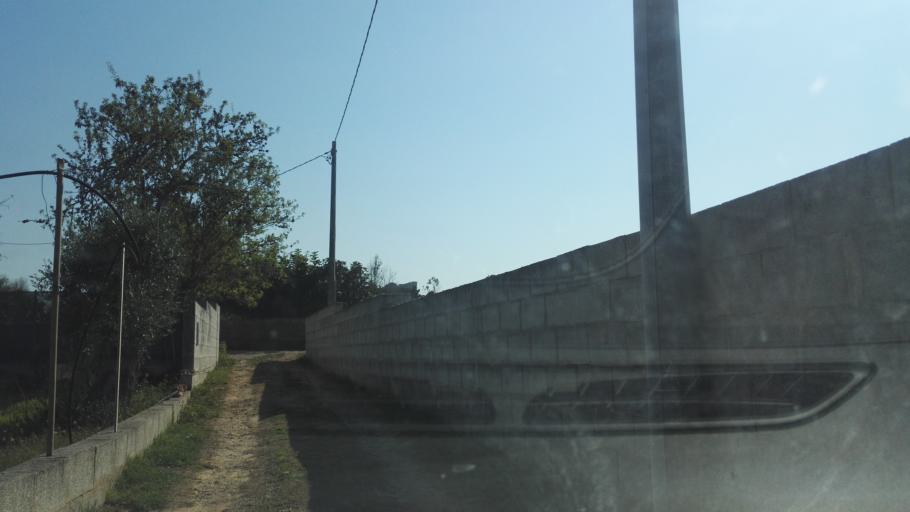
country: IT
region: Apulia
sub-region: Provincia di Lecce
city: Alezio
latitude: 40.0499
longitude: 18.0382
